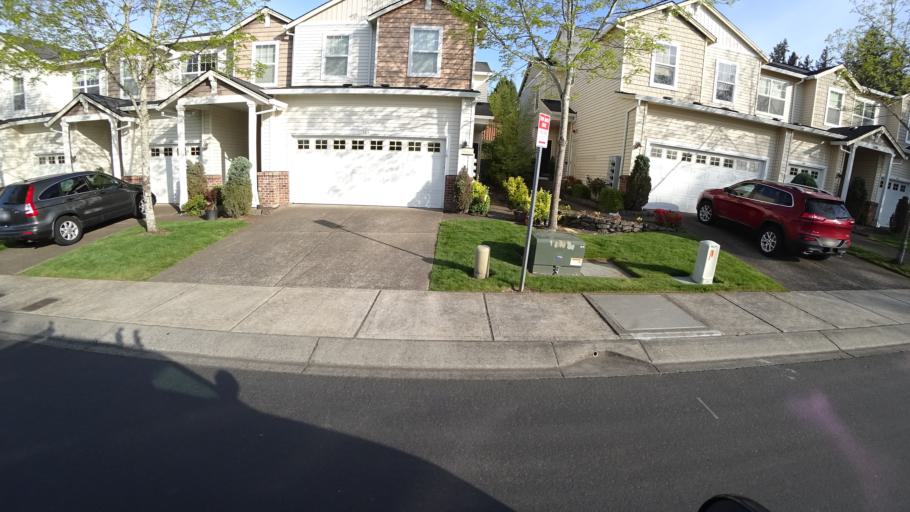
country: US
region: Oregon
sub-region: Washington County
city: King City
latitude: 45.4288
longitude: -122.8435
